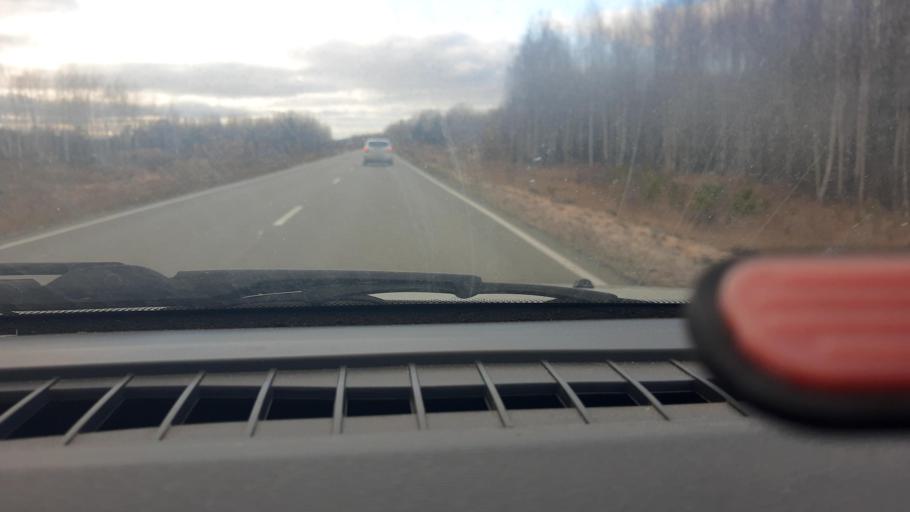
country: RU
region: Nizjnij Novgorod
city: Babino
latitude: 56.2965
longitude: 43.6258
